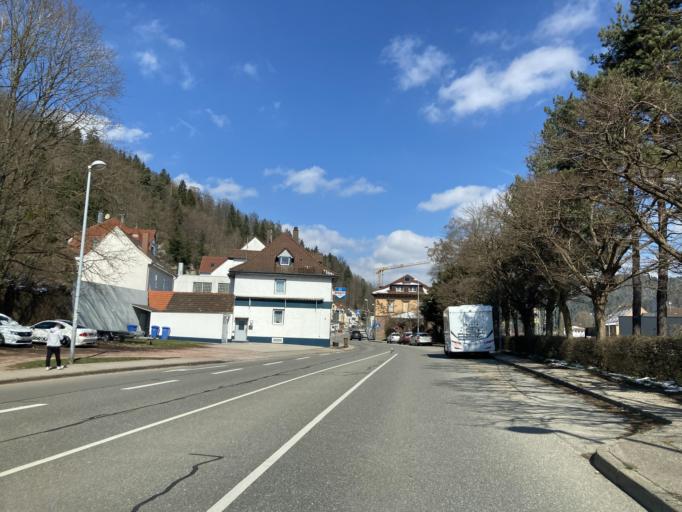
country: DE
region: Baden-Wuerttemberg
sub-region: Freiburg Region
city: Oberndorf
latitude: 48.2937
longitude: 8.5757
